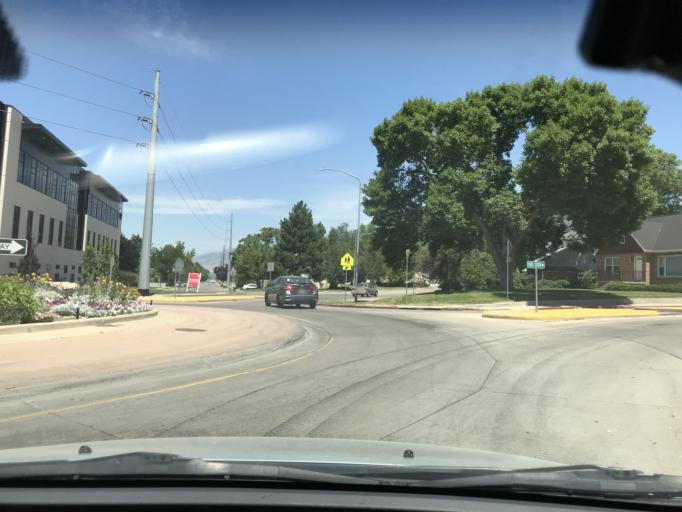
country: US
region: Utah
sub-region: Davis County
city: Woods Cross
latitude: 40.8745
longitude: -111.8856
